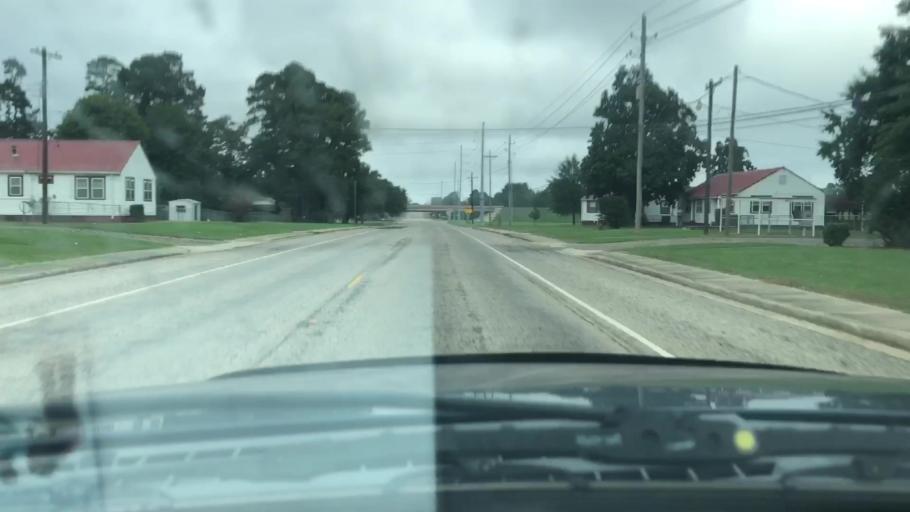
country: US
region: Texas
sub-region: Bowie County
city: Wake Village
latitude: 33.3825
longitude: -94.0921
